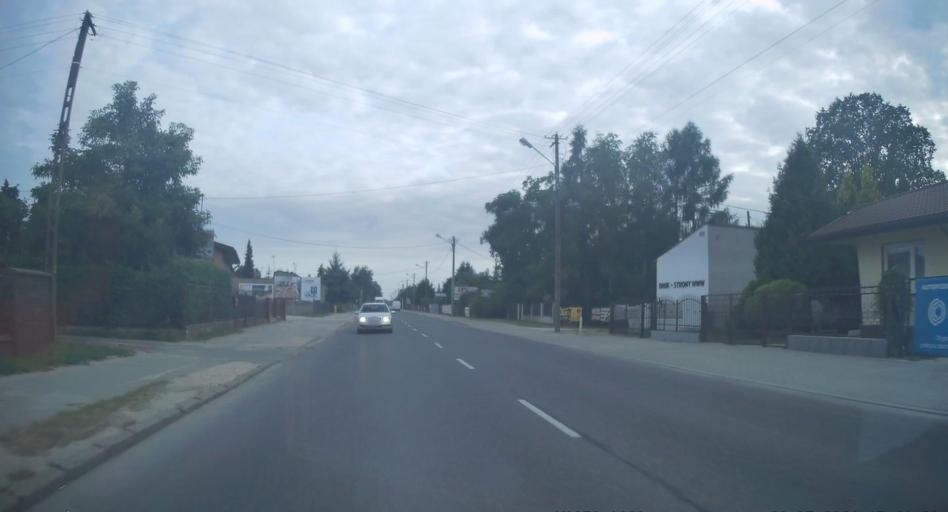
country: PL
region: Lodz Voivodeship
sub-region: Powiat radomszczanski
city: Radomsko
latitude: 51.0872
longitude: 19.4547
